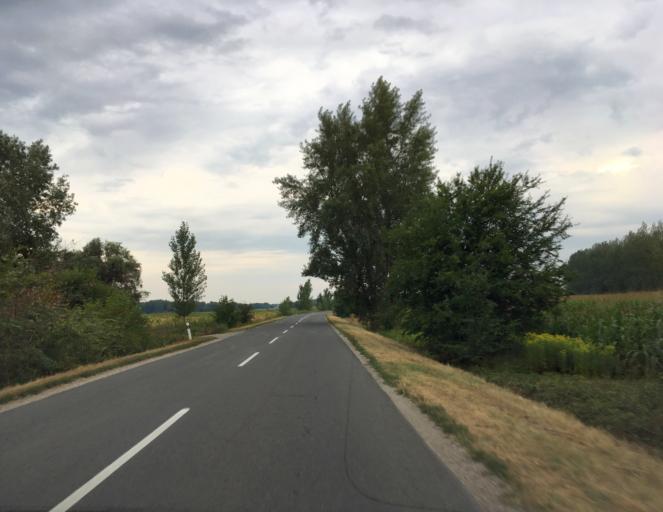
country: SK
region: Trnavsky
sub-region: Okres Dunajska Streda
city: Velky Meder
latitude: 47.9011
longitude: 17.6796
